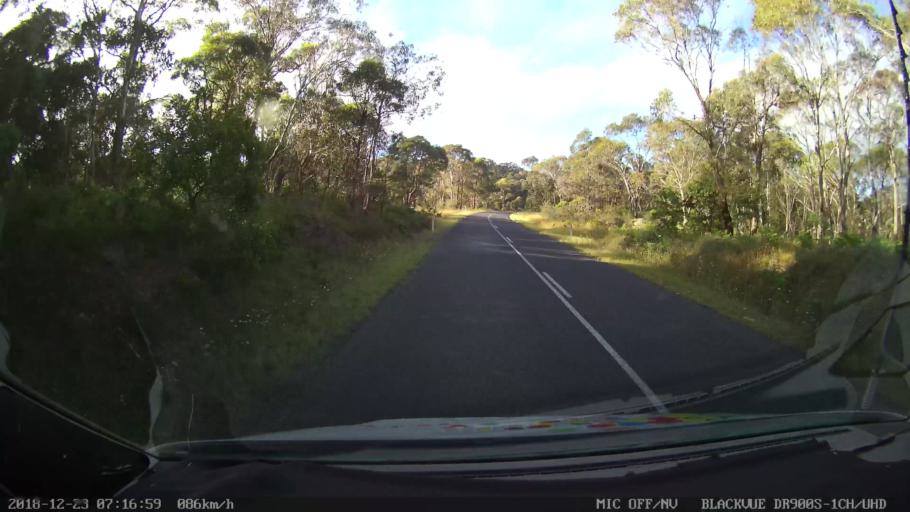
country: AU
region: New South Wales
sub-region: Bellingen
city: Dorrigo
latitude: -30.4629
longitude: 152.3075
